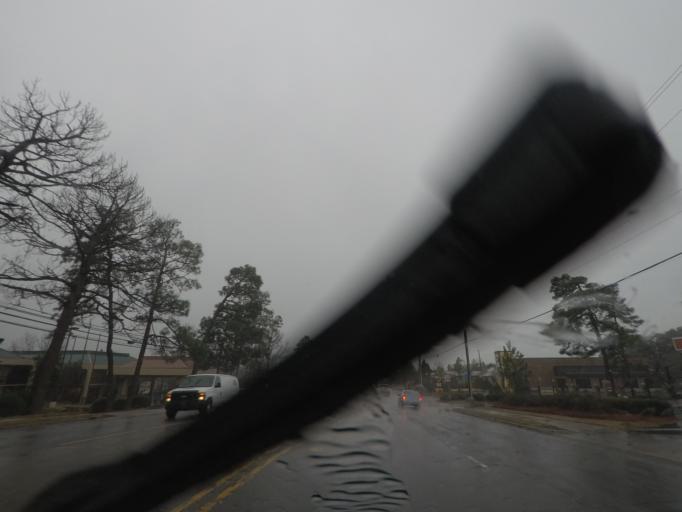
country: US
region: North Carolina
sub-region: Moore County
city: Southern Pines
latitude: 35.1603
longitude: -79.4114
